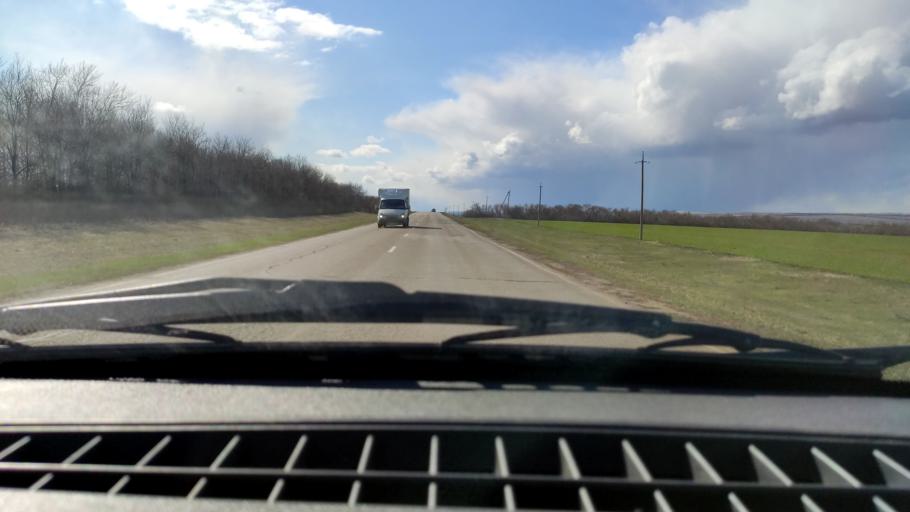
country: RU
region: Bashkortostan
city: Chekmagush
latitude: 55.1066
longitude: 54.9893
